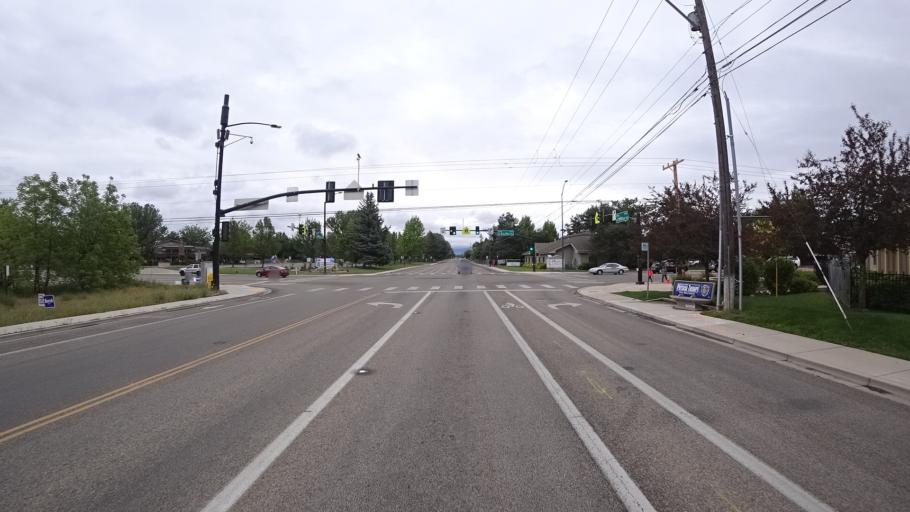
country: US
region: Idaho
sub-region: Ada County
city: Eagle
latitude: 43.6484
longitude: -116.3146
